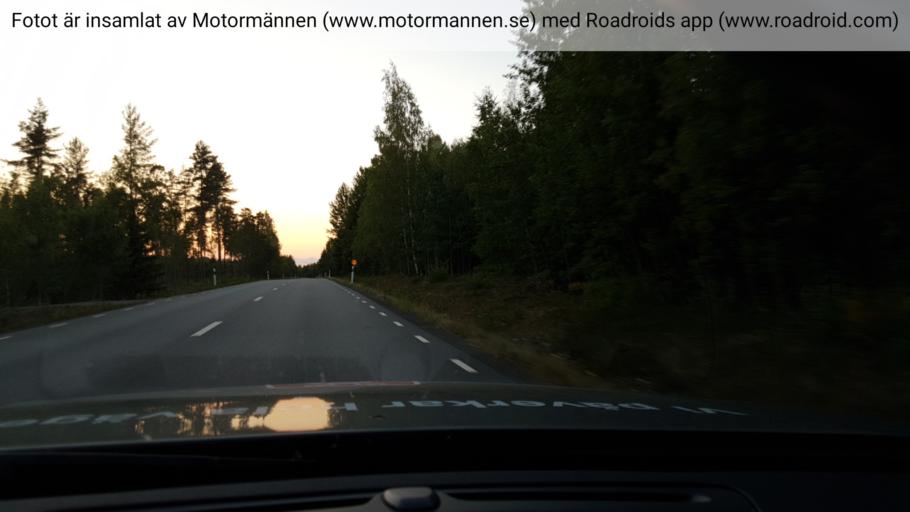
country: SE
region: Uppsala
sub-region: Heby Kommun
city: OEstervala
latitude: 60.1338
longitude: 17.2189
